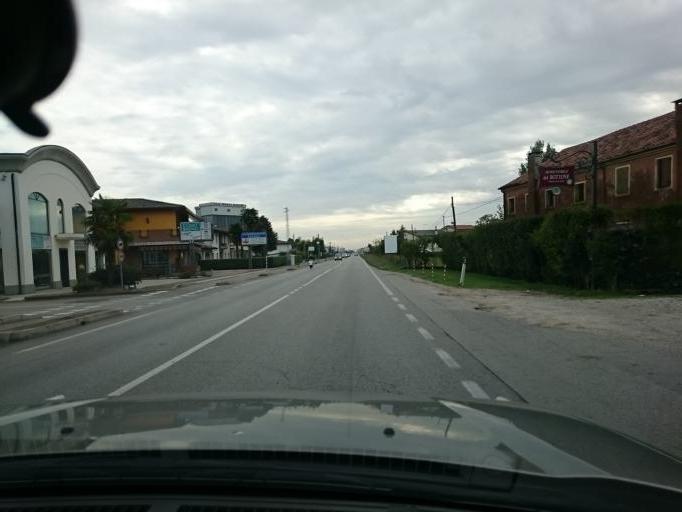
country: IT
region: Veneto
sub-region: Provincia di Padova
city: Sant'Angelo di Piove di Sacco
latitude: 45.3211
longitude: 11.9996
